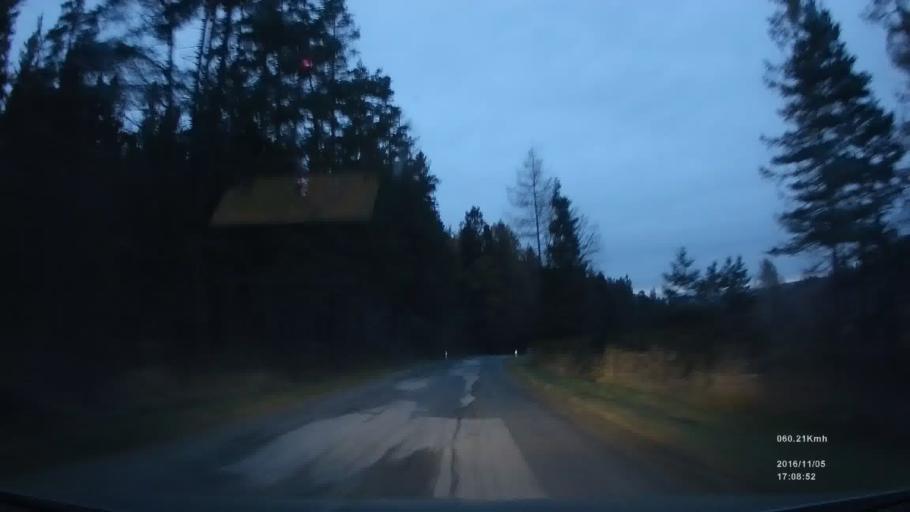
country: SK
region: Presovsky
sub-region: Okres Presov
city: Levoca
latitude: 49.0494
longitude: 20.5185
